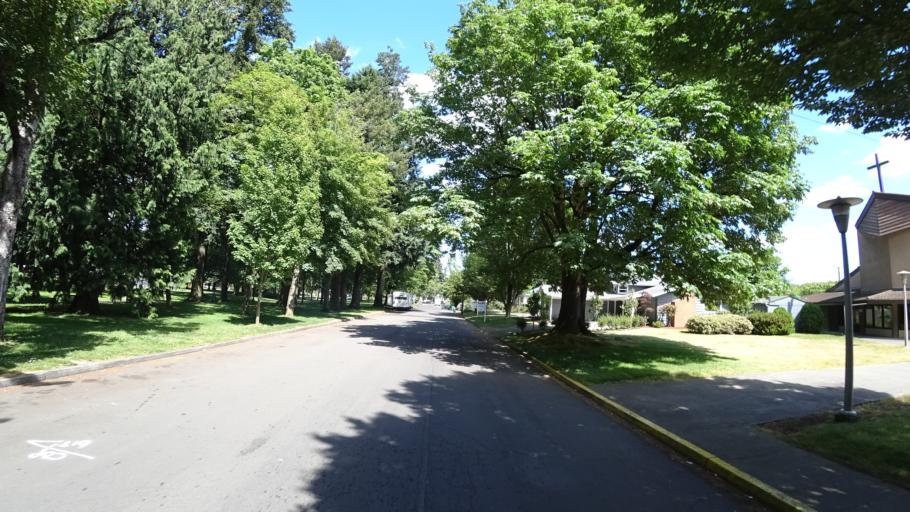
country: US
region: Oregon
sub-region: Multnomah County
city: Portland
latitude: 45.5780
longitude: -122.7105
